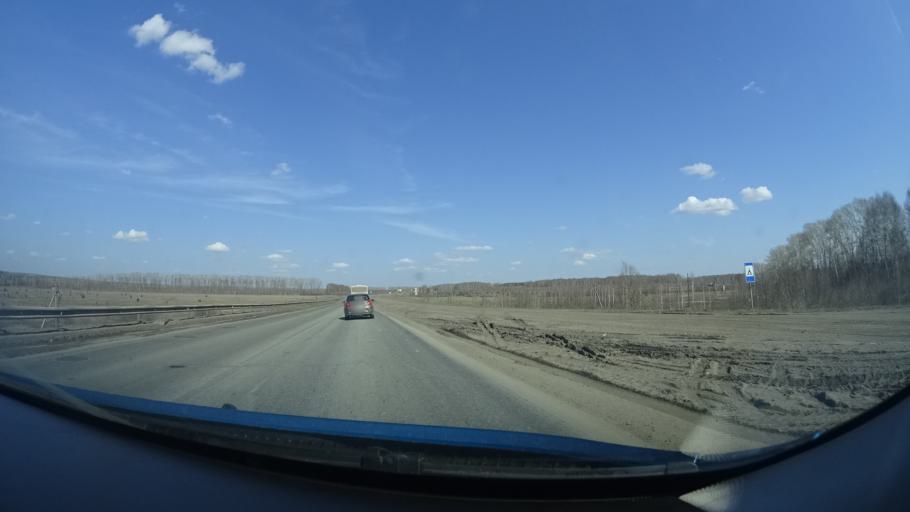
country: RU
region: Bashkortostan
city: Kandry
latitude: 54.6012
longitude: 54.2923
